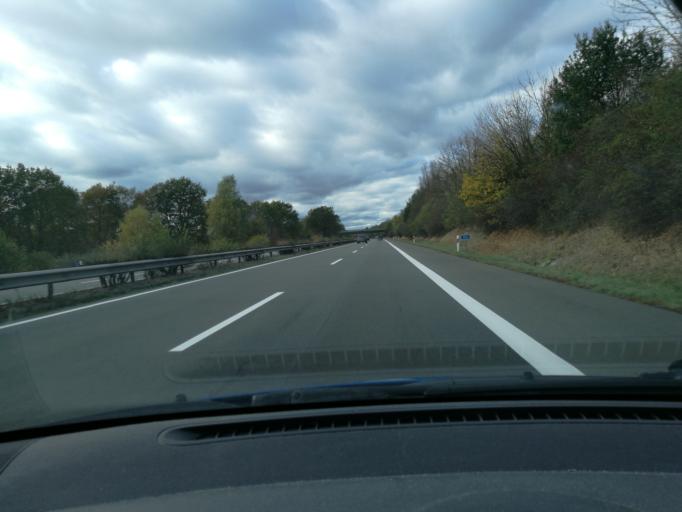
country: DE
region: Lower Saxony
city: Radbruch
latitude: 53.3216
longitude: 10.3030
